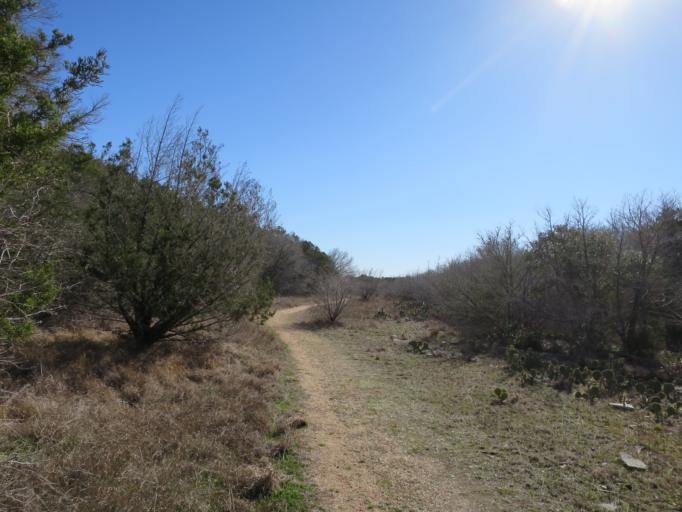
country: US
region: Texas
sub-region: Llano County
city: Kingsland
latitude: 30.6837
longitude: -98.3552
